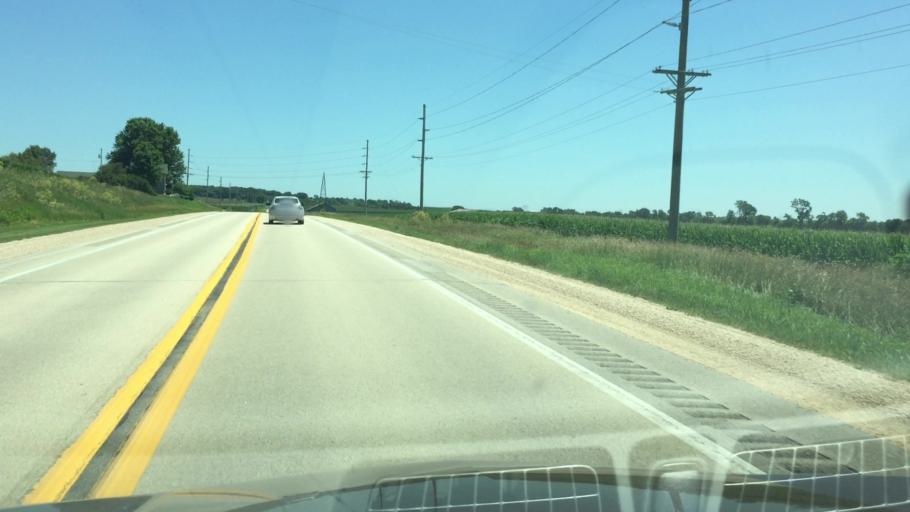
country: US
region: Iowa
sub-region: Jackson County
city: Maquoketa
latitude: 42.0668
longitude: -90.7793
